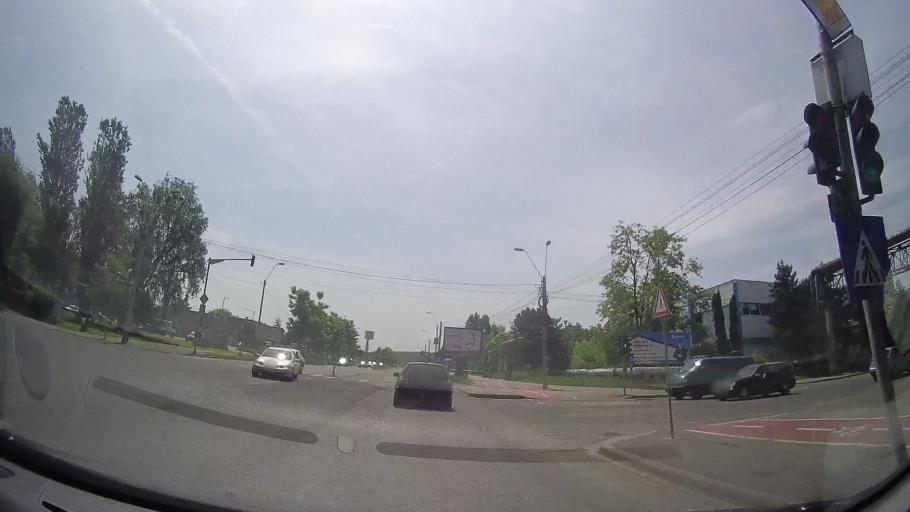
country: RO
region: Hunedoara
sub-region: Municipiul Deva
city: Deva
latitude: 45.8748
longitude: 22.9166
